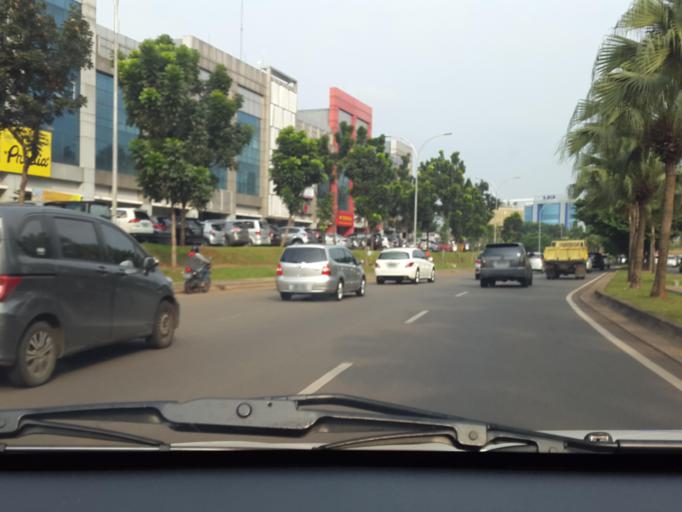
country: ID
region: Banten
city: South Tangerang
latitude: -6.2727
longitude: 106.7152
